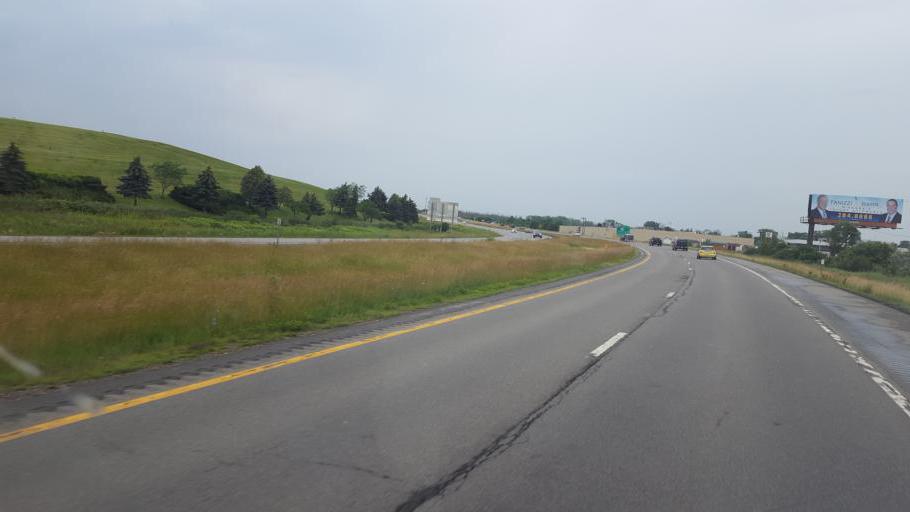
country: US
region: New York
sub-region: Niagara County
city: Niagara Falls
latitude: 43.1036
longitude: -78.9826
